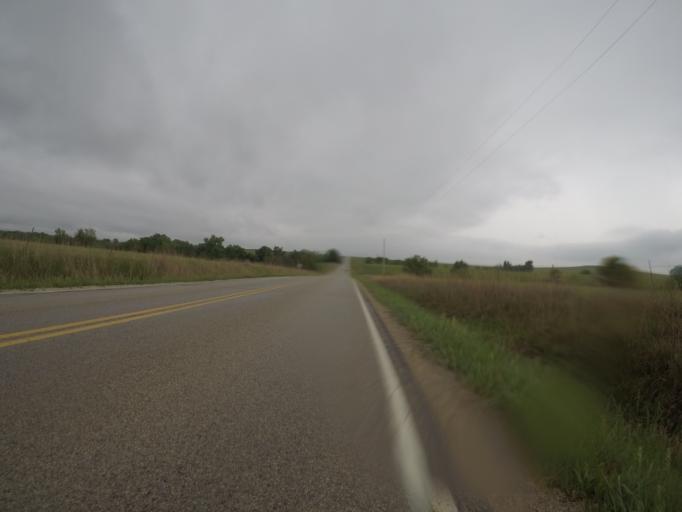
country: US
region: Kansas
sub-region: Pottawatomie County
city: Westmoreland
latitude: 39.4337
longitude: -96.1839
